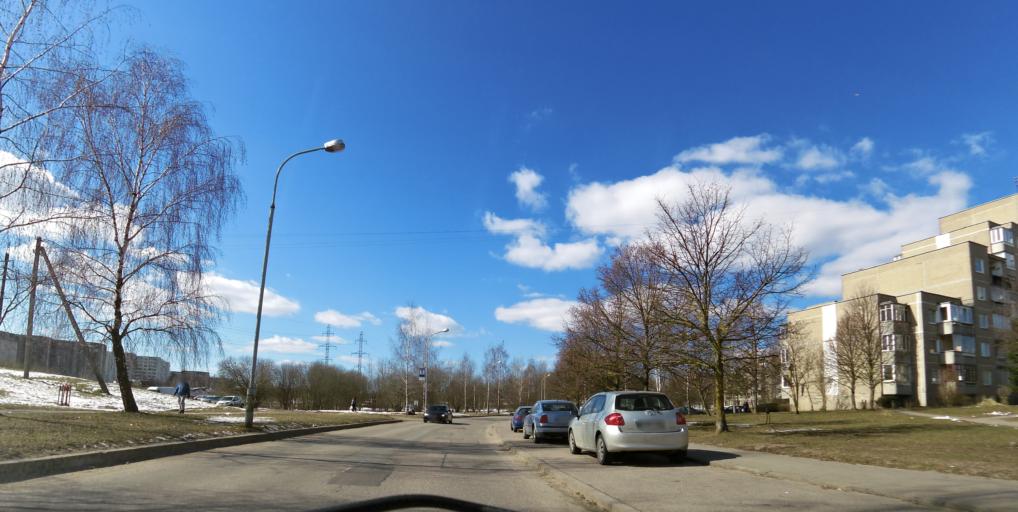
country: LT
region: Vilnius County
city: Justiniskes
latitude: 54.7236
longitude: 25.2289
